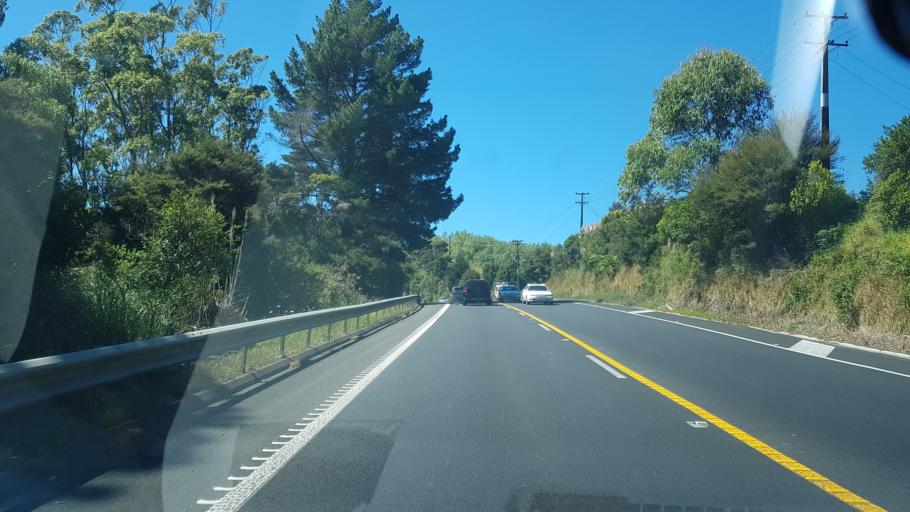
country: NZ
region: Auckland
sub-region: Auckland
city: Warkworth
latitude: -36.4645
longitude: 174.6509
